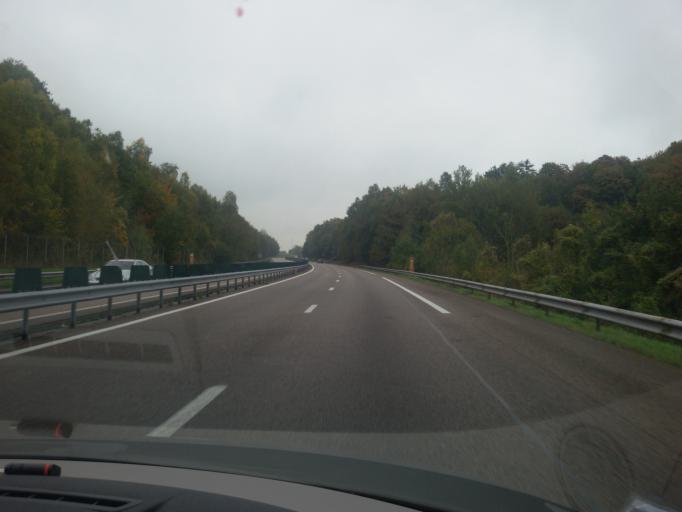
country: FR
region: Haute-Normandie
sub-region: Departement de l'Eure
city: Pont-Audemer
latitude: 49.3875
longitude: 0.5092
